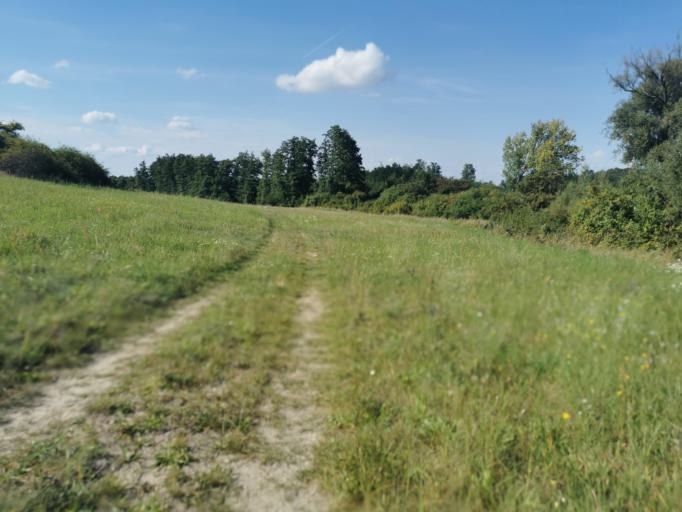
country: SK
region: Trnavsky
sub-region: Okres Senica
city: Senica
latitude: 48.6089
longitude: 17.2365
